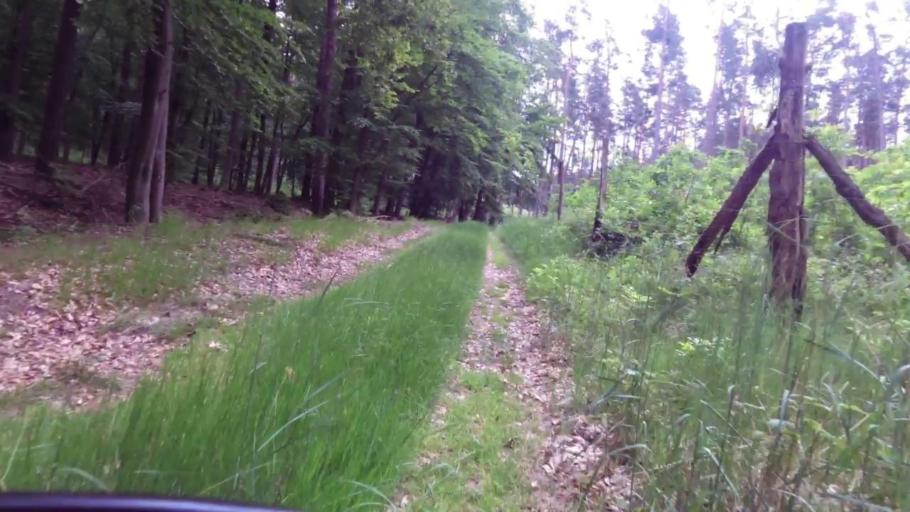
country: PL
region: West Pomeranian Voivodeship
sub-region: Powiat kamienski
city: Miedzyzdroje
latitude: 53.8678
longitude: 14.5132
